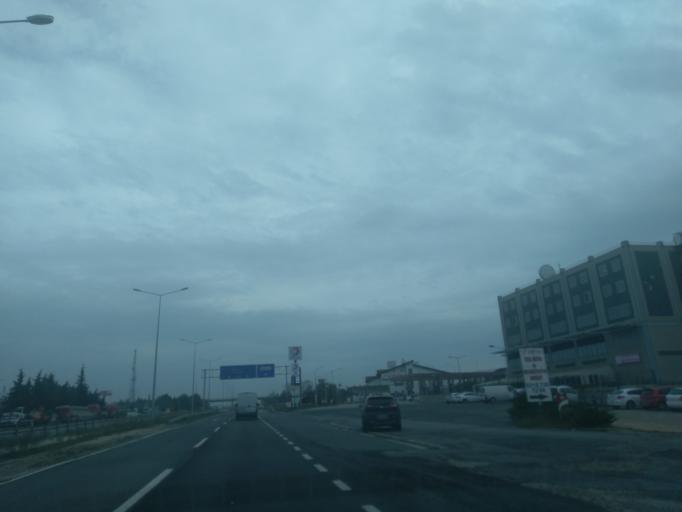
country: TR
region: Istanbul
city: Silivri
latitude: 41.0804
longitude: 28.2072
